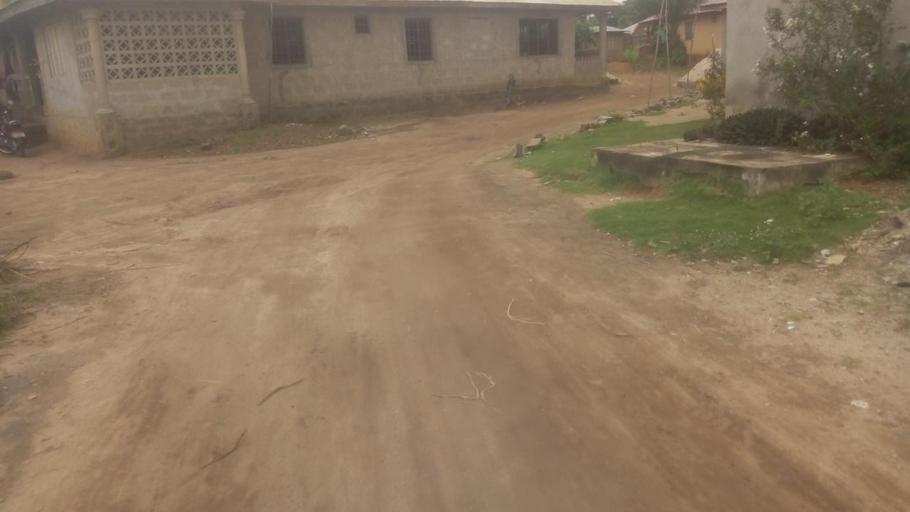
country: SL
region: Northern Province
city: Masoyila
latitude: 8.6053
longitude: -13.1891
